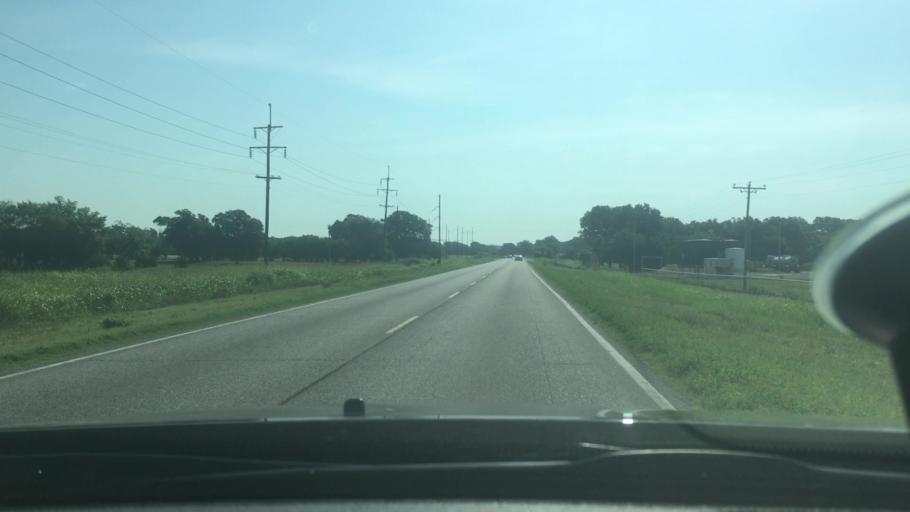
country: US
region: Oklahoma
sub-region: Garvin County
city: Wynnewood
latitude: 34.6516
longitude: -97.2098
